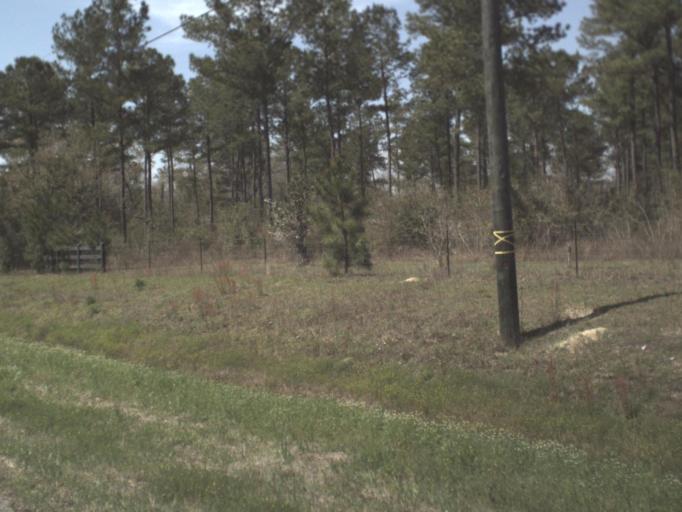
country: US
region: Florida
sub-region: Gadsden County
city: Quincy
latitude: 30.5542
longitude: -84.5210
